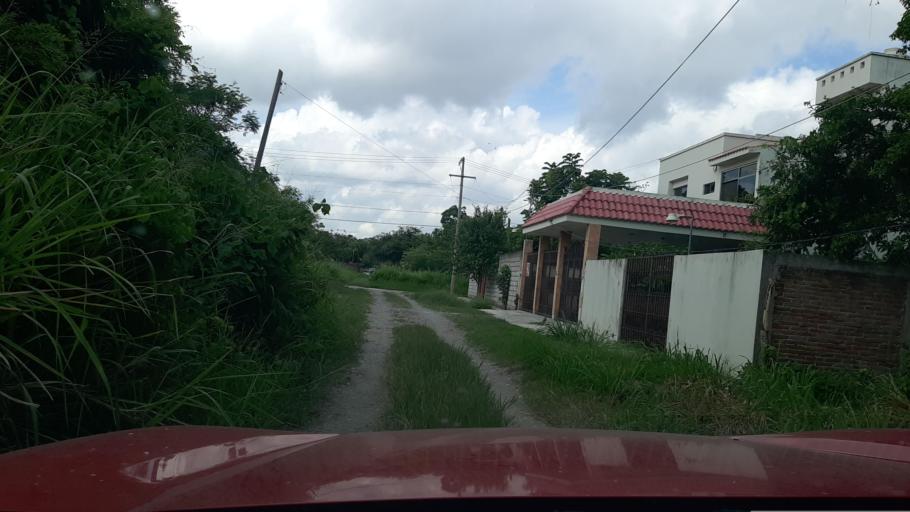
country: MX
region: Veracruz
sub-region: Poza Rica de Hidalgo
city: Villa de las Flores
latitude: 20.5734
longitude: -97.4345
